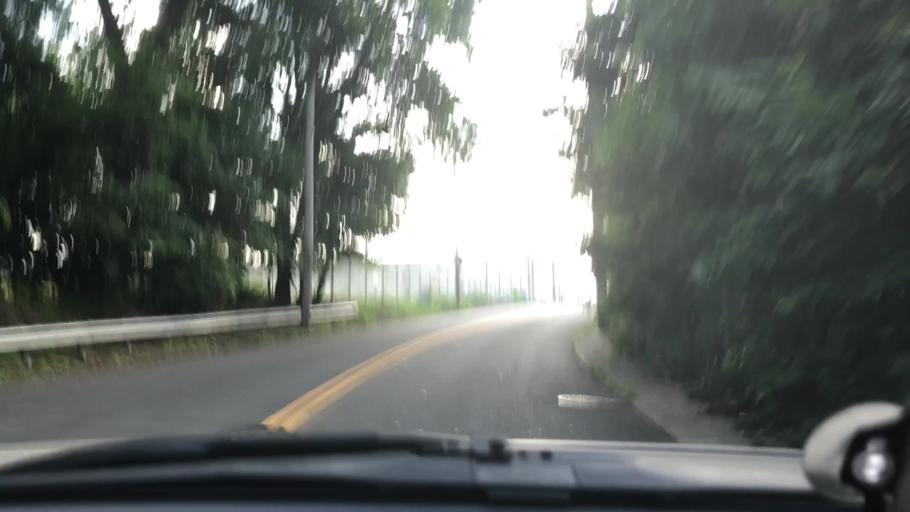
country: US
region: New York
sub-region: Richmond County
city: Bloomfield
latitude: 40.6410
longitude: -74.1777
